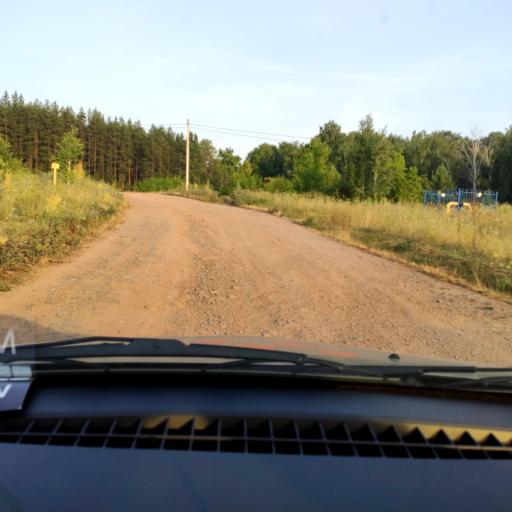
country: RU
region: Bashkortostan
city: Avdon
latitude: 54.5863
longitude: 55.6805
